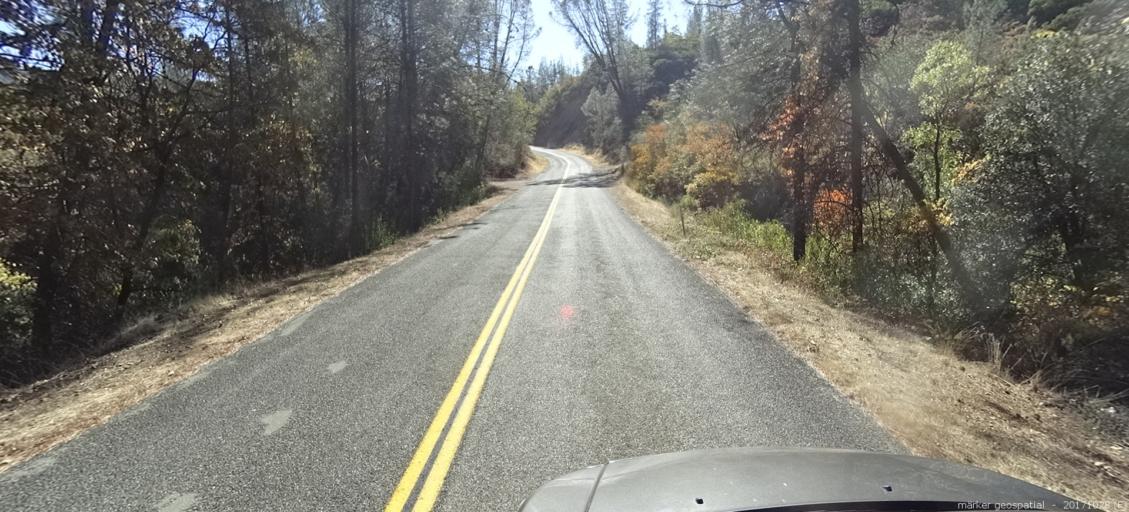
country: US
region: California
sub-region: Shasta County
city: Shasta
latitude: 40.6456
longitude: -122.5576
